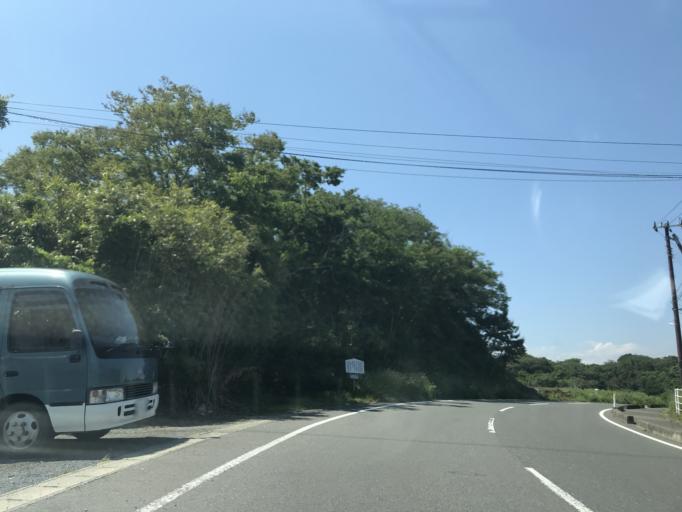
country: JP
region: Miyagi
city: Matsushima
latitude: 38.3264
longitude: 141.1552
